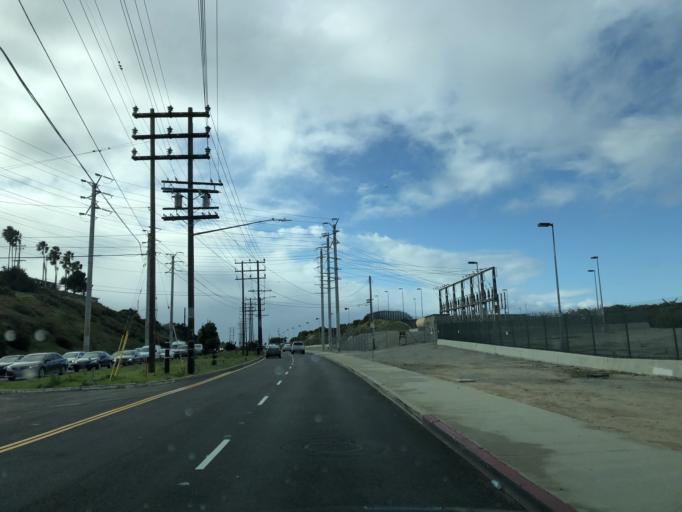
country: US
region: California
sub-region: Los Angeles County
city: El Segundo
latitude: 33.9314
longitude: -118.4248
